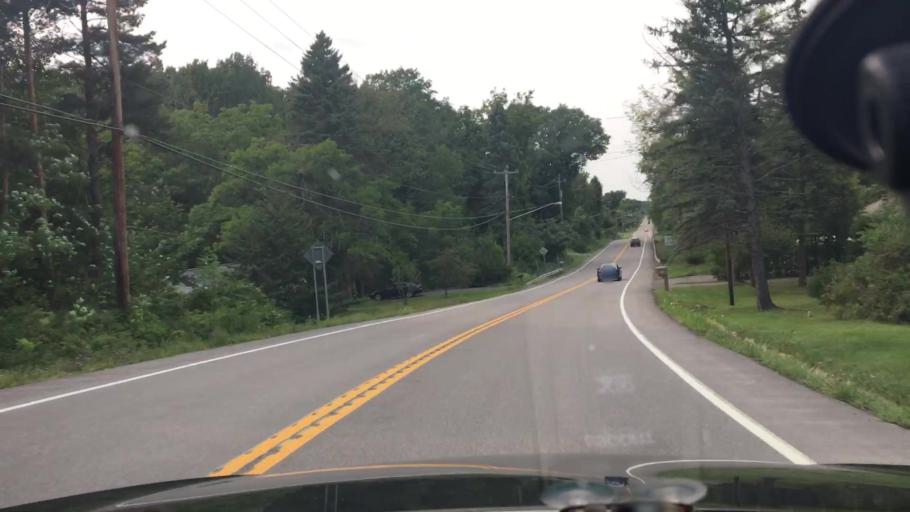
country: US
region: New York
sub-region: Erie County
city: Orchard Park
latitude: 42.7351
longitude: -78.7324
